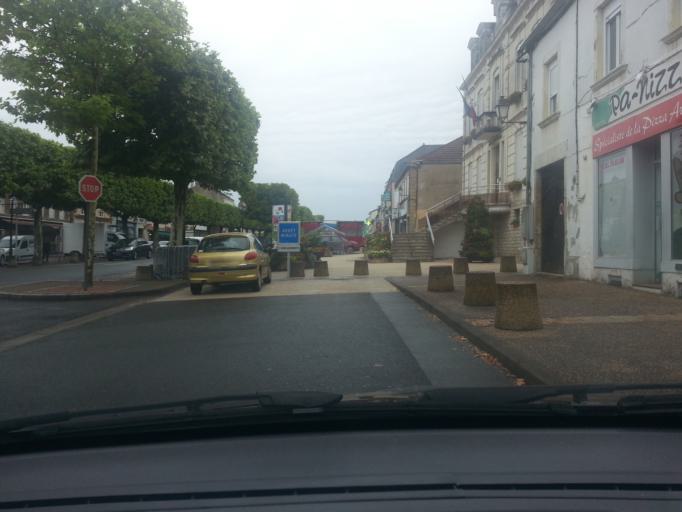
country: FR
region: Bourgogne
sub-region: Departement de Saone-et-Loire
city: Montchanin
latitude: 46.7478
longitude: 4.4698
